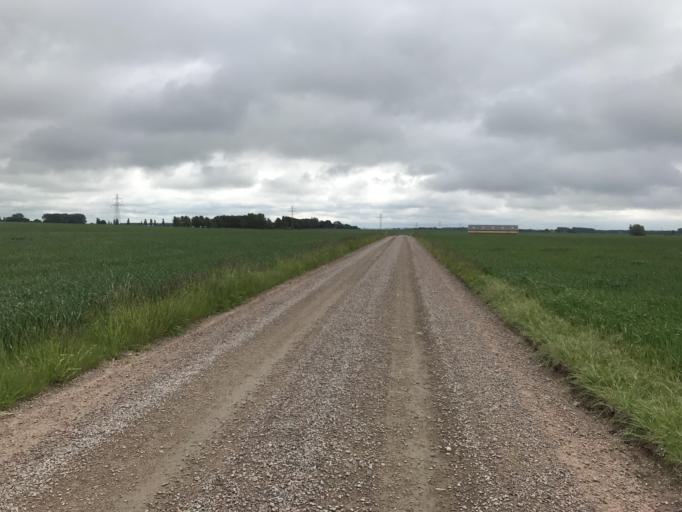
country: SE
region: Skane
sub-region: Landskrona
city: Asmundtorp
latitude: 55.8724
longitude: 12.8909
